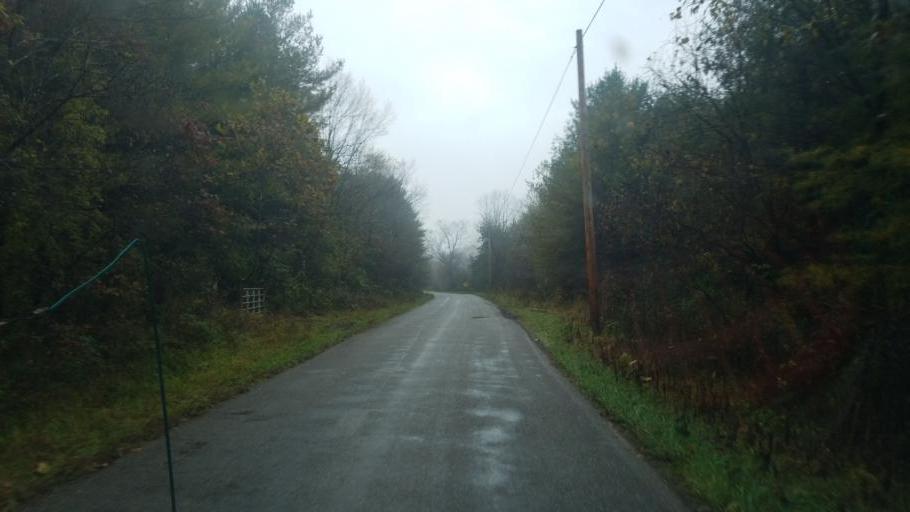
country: US
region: Ohio
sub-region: Athens County
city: Glouster
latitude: 39.4575
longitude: -81.9296
